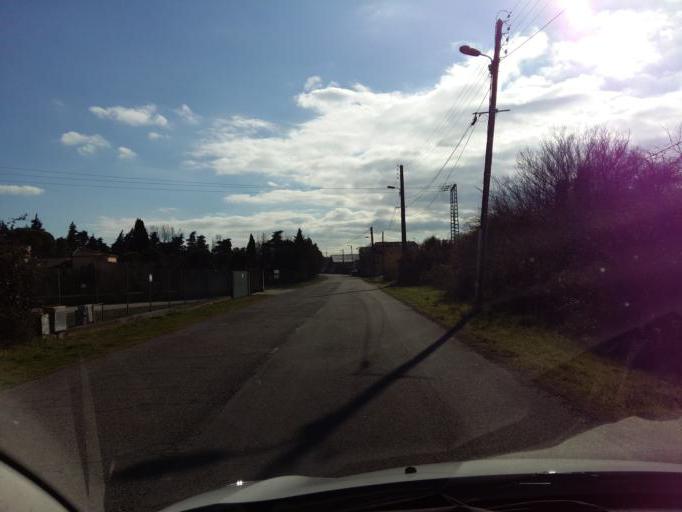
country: FR
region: Provence-Alpes-Cote d'Azur
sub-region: Departement du Vaucluse
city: Cavaillon
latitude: 43.8259
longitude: 5.0468
